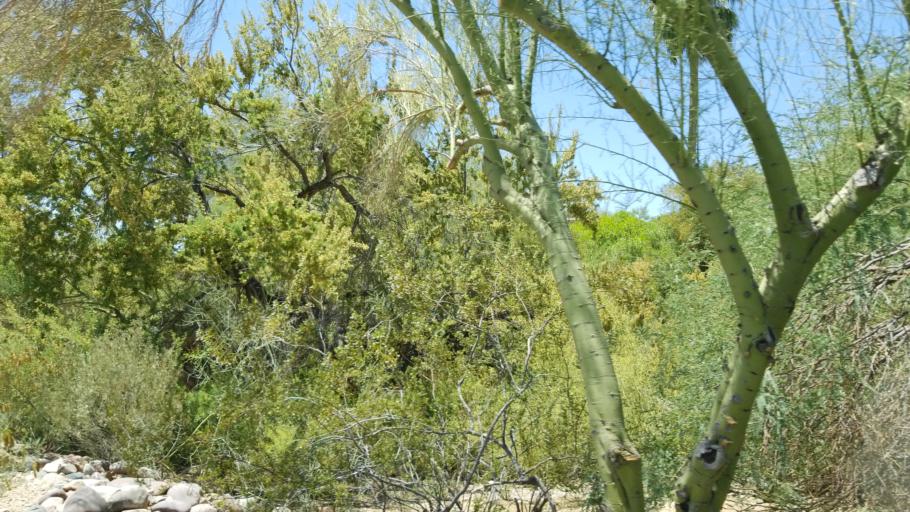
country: US
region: Arizona
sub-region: Maricopa County
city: Paradise Valley
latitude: 33.5256
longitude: -111.9812
